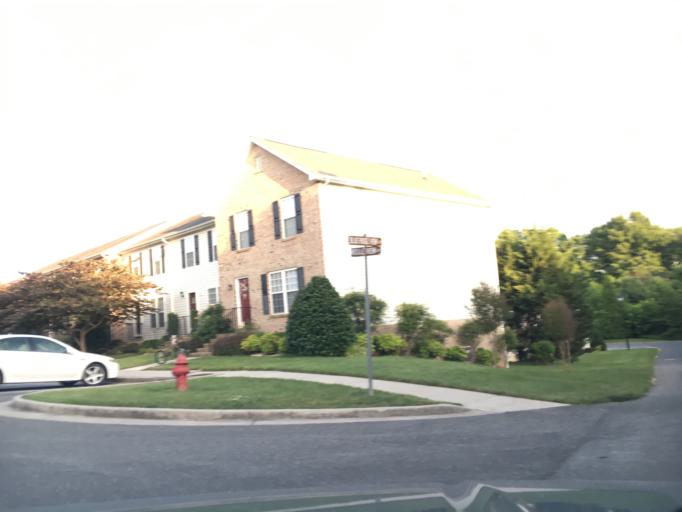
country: US
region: Virginia
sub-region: Bedford County
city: Forest
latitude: 37.3676
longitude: -79.3078
